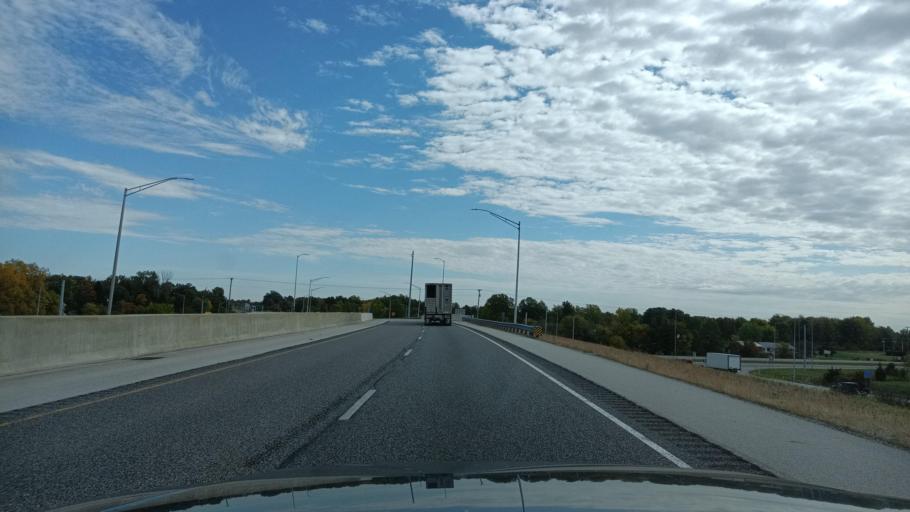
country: US
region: Indiana
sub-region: Allen County
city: New Haven
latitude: 40.9822
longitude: -85.0881
